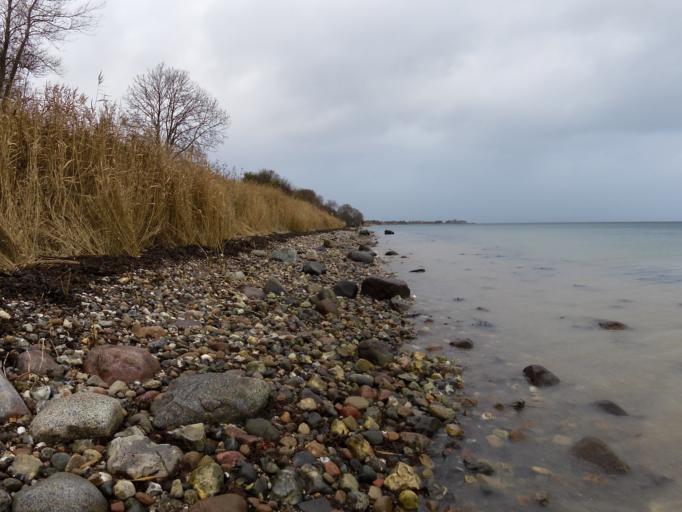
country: DK
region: Central Jutland
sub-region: Arhus Kommune
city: Malling
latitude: 56.0016
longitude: 10.2626
